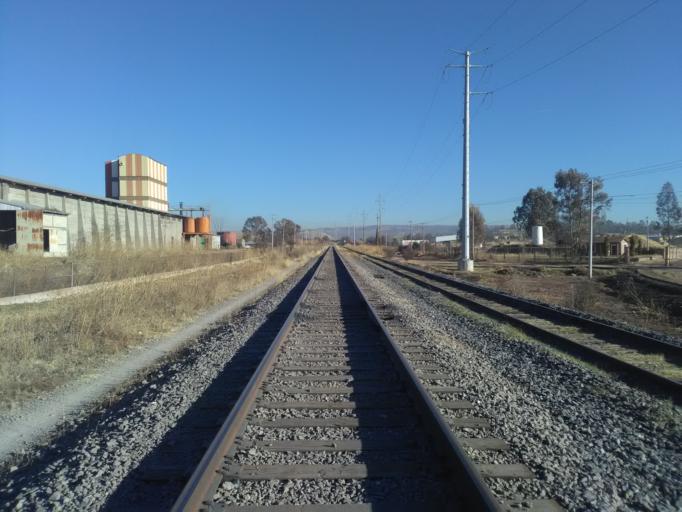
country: MX
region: Durango
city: Victoria de Durango
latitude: 24.0592
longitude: -104.6542
